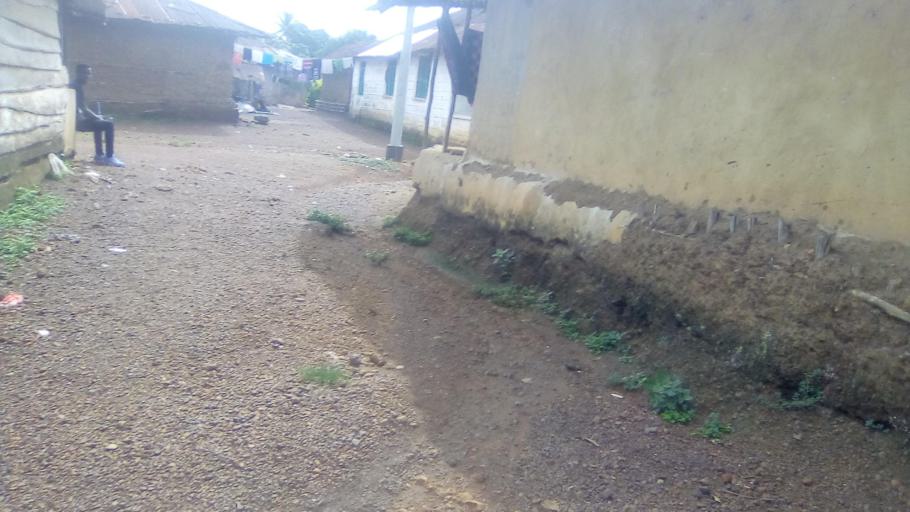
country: SL
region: Southern Province
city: Moyamba
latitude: 8.1555
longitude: -12.4290
